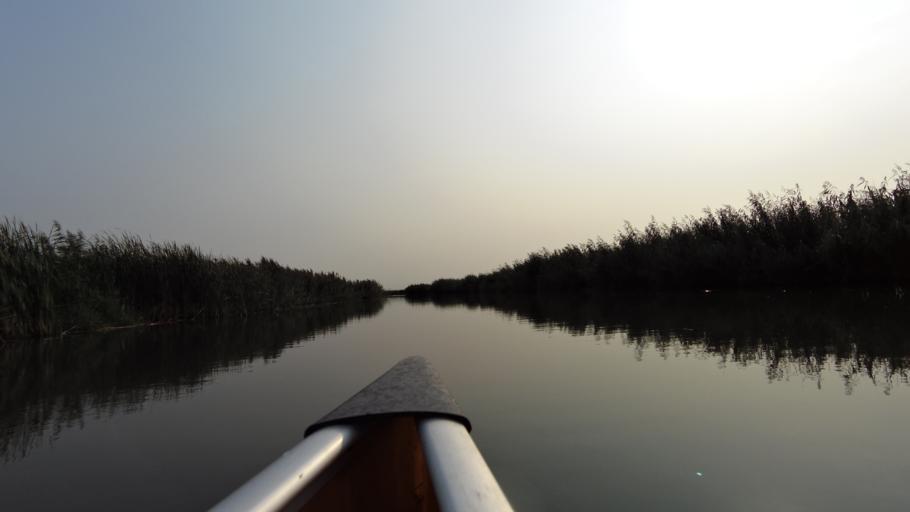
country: NL
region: South Holland
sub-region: Gemeente Sliedrecht
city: Sliedrecht
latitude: 51.7815
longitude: 4.8174
